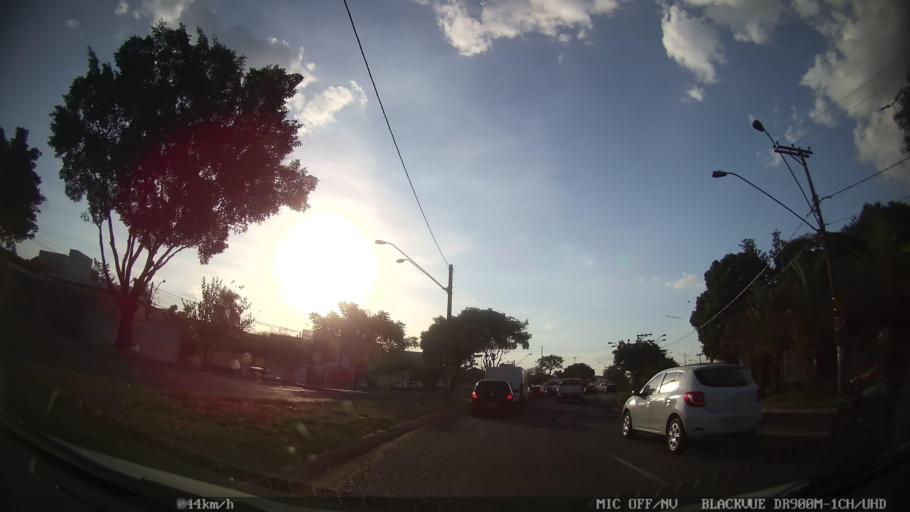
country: BR
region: Sao Paulo
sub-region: Ribeirao Preto
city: Ribeirao Preto
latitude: -21.1660
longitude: -47.8163
